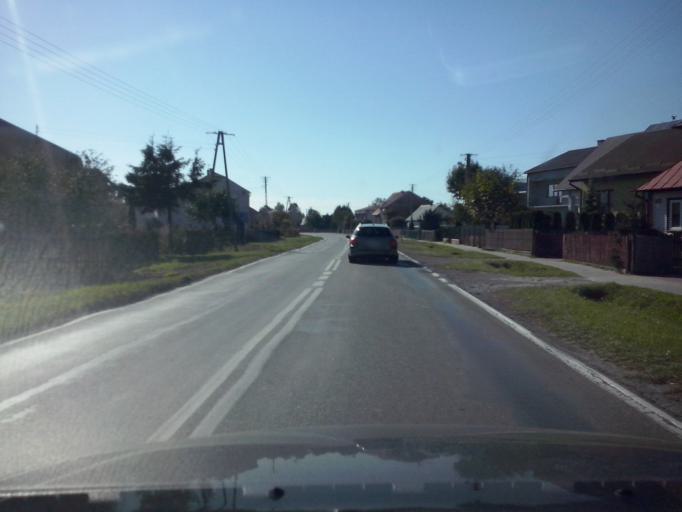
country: PL
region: Lublin Voivodeship
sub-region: Powiat bilgorajski
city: Bilgoraj
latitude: 50.5098
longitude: 22.6482
